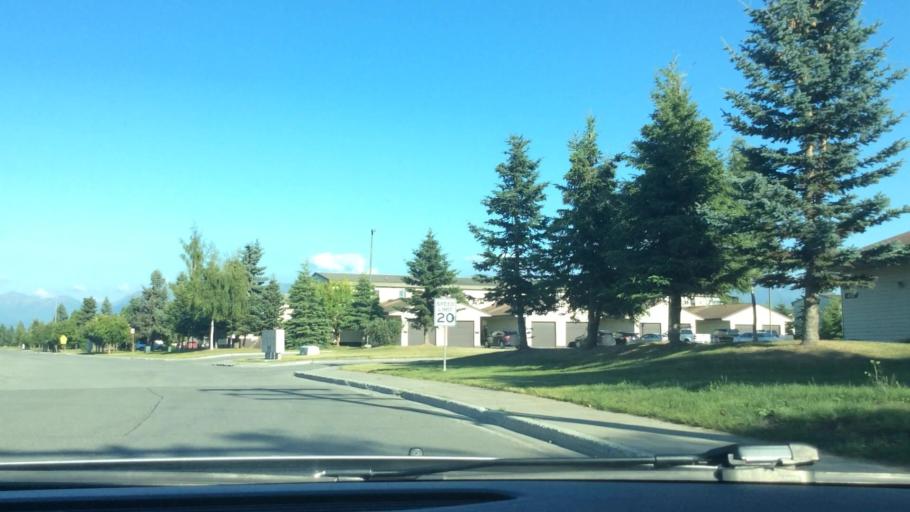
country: US
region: Alaska
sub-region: Anchorage Municipality
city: Anchorage
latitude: 61.2332
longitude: -149.8592
